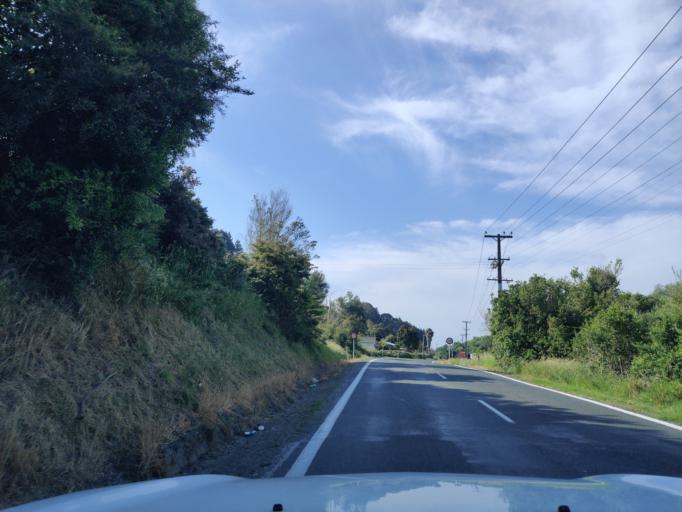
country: NZ
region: Waikato
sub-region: Waikato District
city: Ngaruawahia
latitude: -37.5844
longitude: 175.1543
